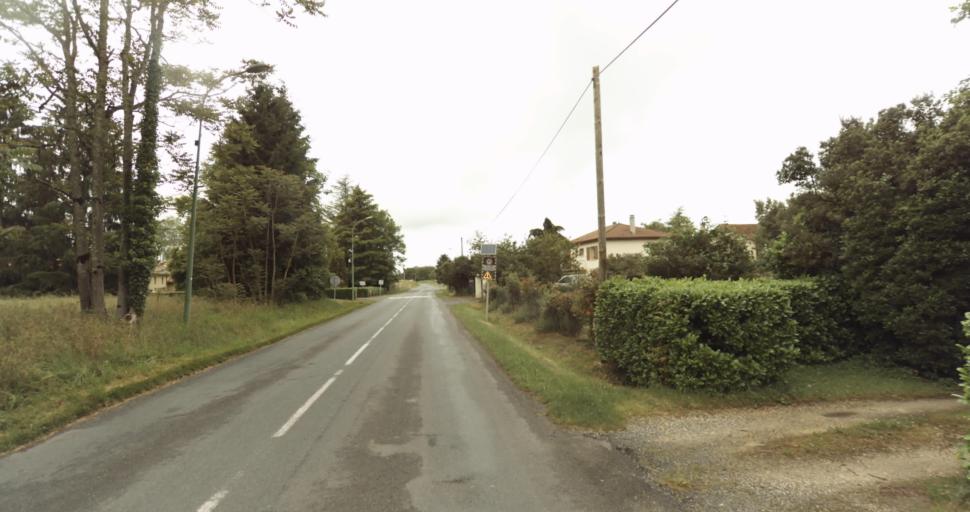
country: FR
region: Aquitaine
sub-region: Departement de la Dordogne
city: Beaumont-du-Perigord
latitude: 44.6886
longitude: 0.8857
